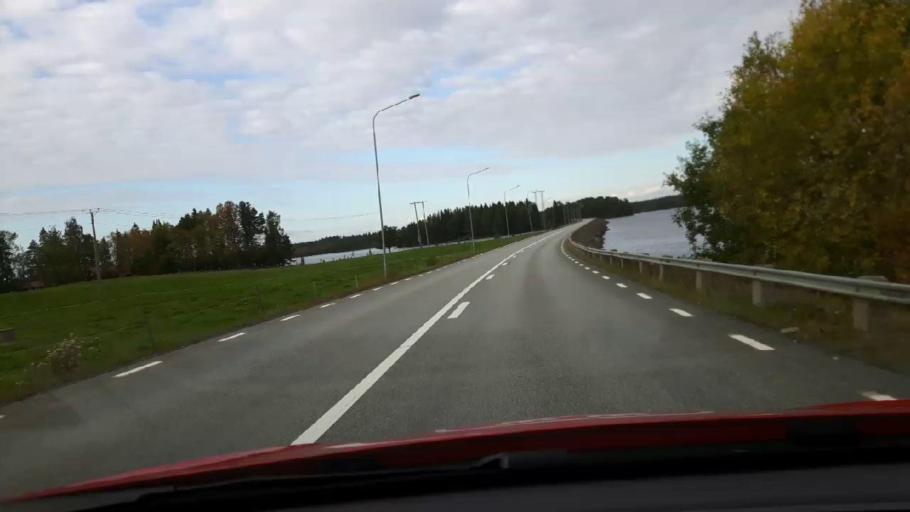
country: SE
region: Jaemtland
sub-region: Krokoms Kommun
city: Valla
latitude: 63.2439
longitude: 13.9995
